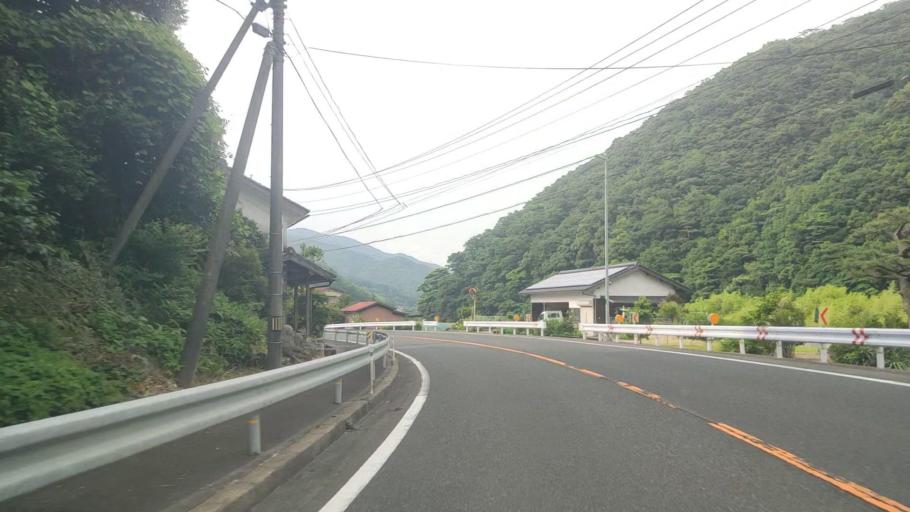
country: JP
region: Tottori
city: Kurayoshi
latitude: 35.3362
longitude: 133.8413
